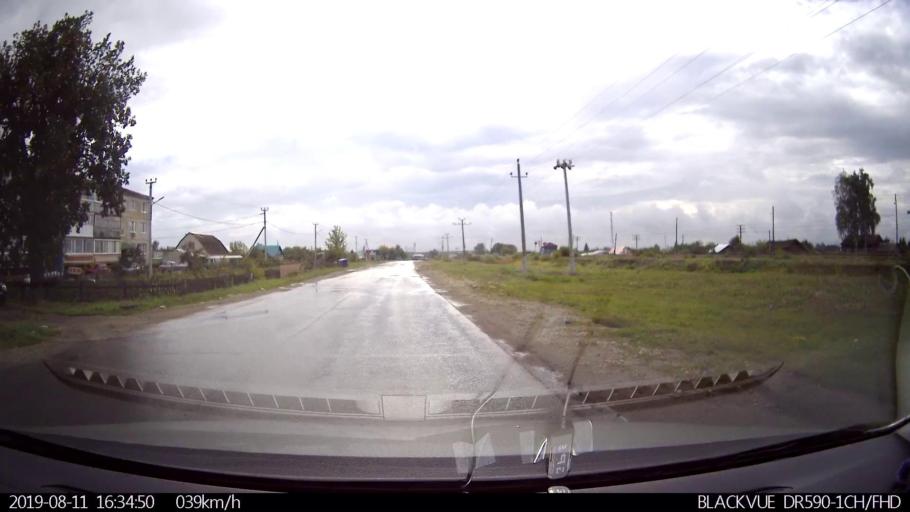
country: RU
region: Ulyanovsk
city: Mayna
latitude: 54.1155
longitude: 47.6183
